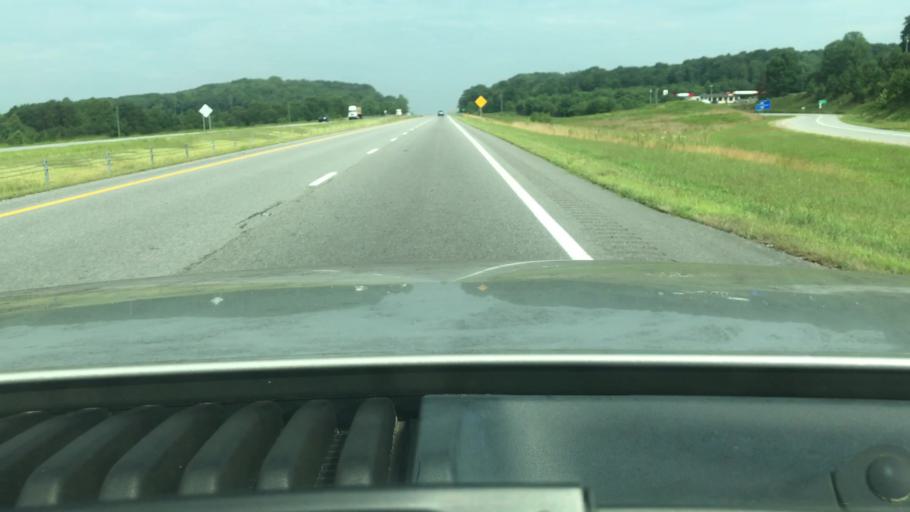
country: US
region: North Carolina
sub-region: Yadkin County
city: Jonesville
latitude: 36.1530
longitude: -80.9278
